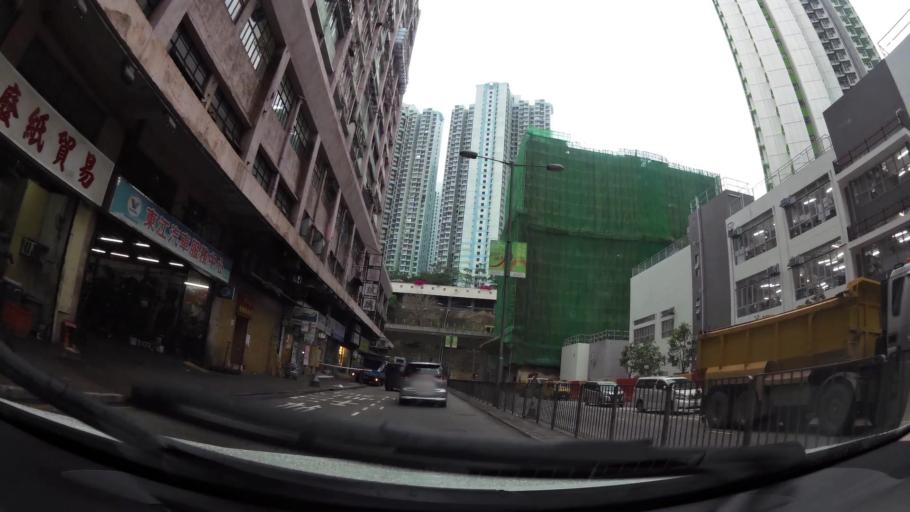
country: HK
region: Tsuen Wan
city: Tsuen Wan
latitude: 22.3678
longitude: 114.1206
